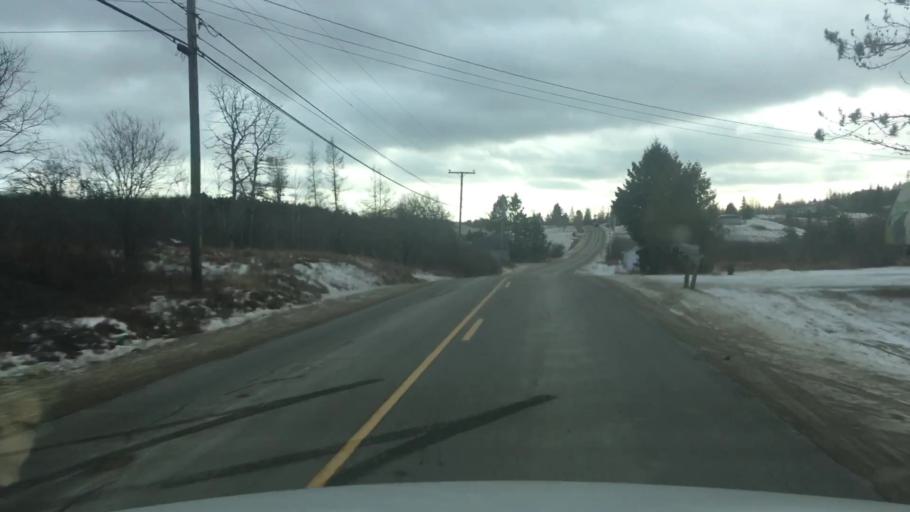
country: US
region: Maine
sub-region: Washington County
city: Machias
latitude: 44.6793
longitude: -67.4675
